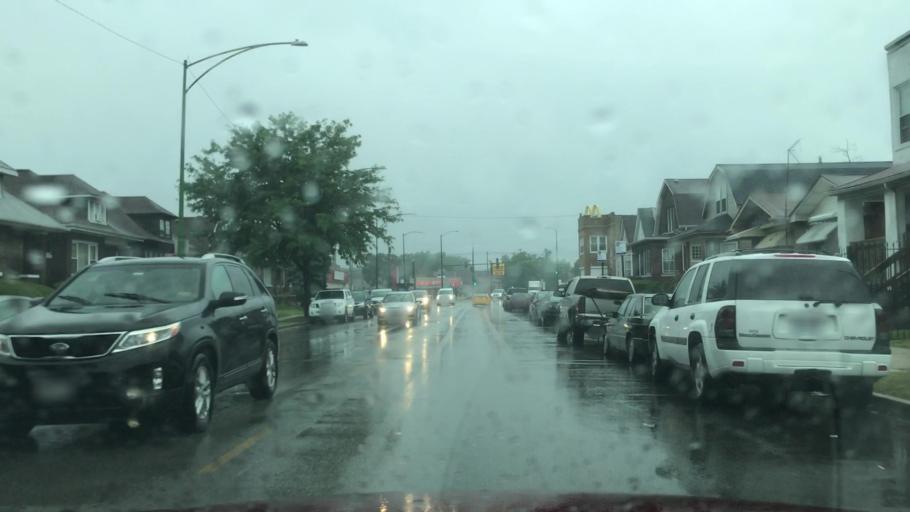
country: US
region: Illinois
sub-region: Cook County
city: Oak Park
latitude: 41.9080
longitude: -87.7559
